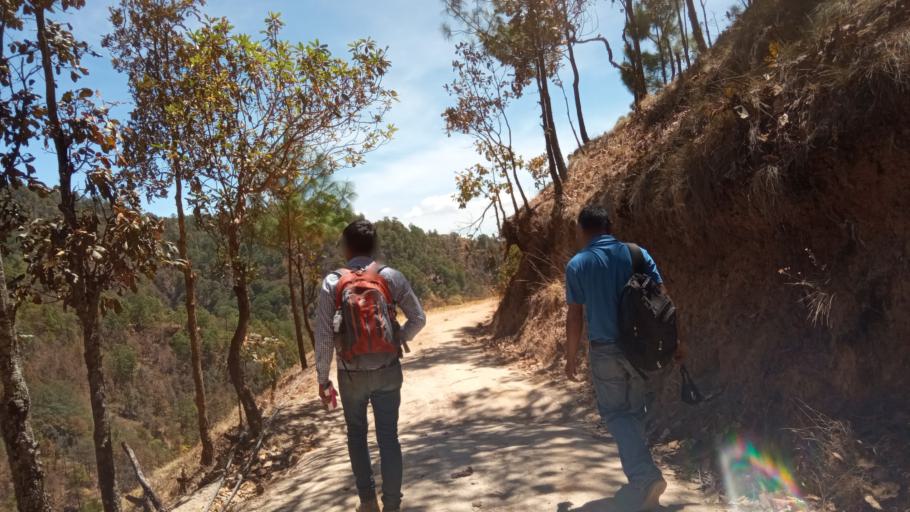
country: GT
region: San Marcos
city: Tejutla
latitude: 15.1316
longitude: -91.7928
